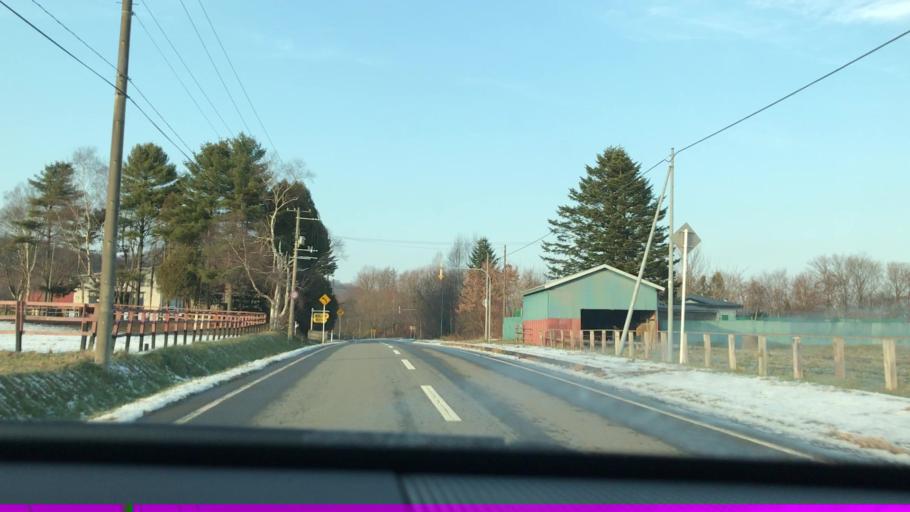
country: JP
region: Hokkaido
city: Shizunai-furukawacho
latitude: 42.4275
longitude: 142.4037
